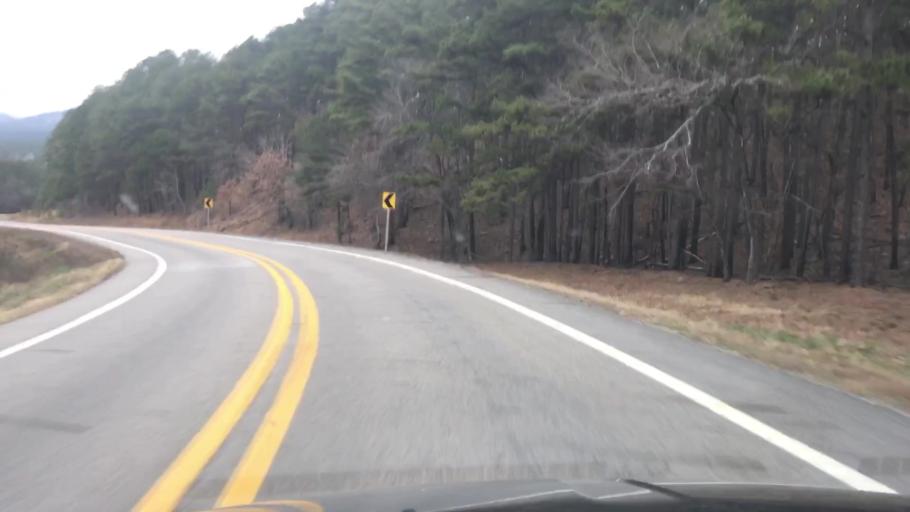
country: US
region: Arkansas
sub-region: Montgomery County
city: Mount Ida
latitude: 34.6834
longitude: -93.7985
